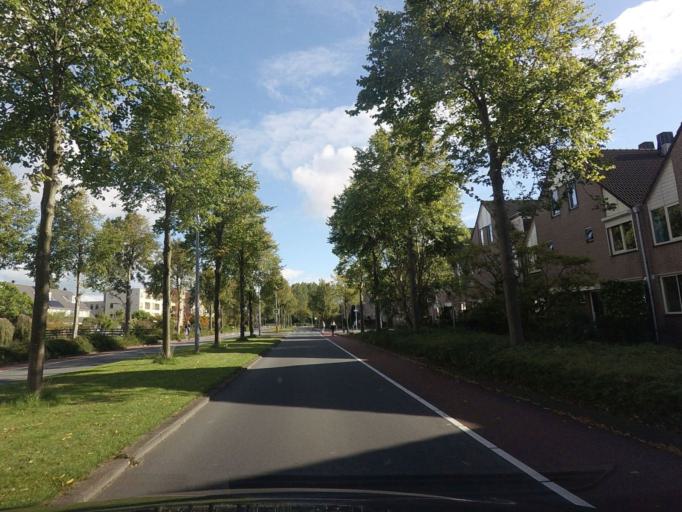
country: NL
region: North Holland
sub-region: Gemeente Langedijk
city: Broek op Langedijk
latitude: 52.6712
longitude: 4.7712
